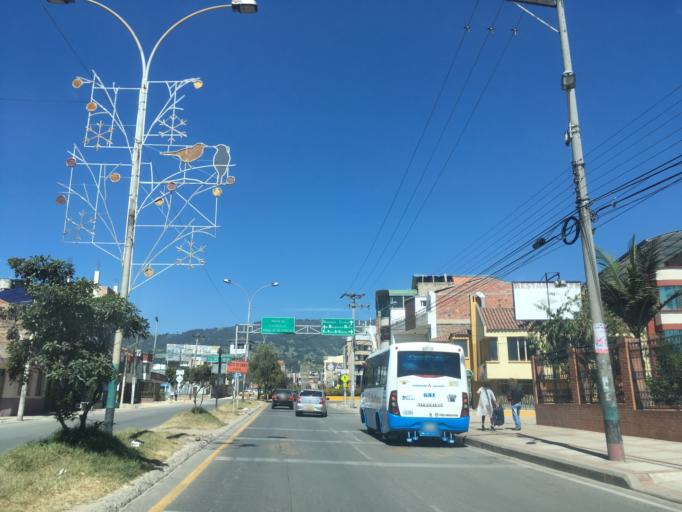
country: CO
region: Boyaca
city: Duitama
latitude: 5.8229
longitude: -73.0263
